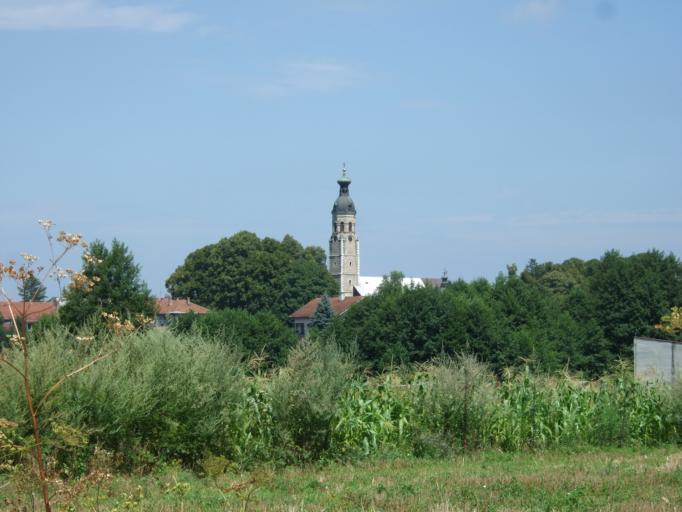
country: HR
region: Karlovacka
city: Plaski
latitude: 45.0780
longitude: 15.3648
